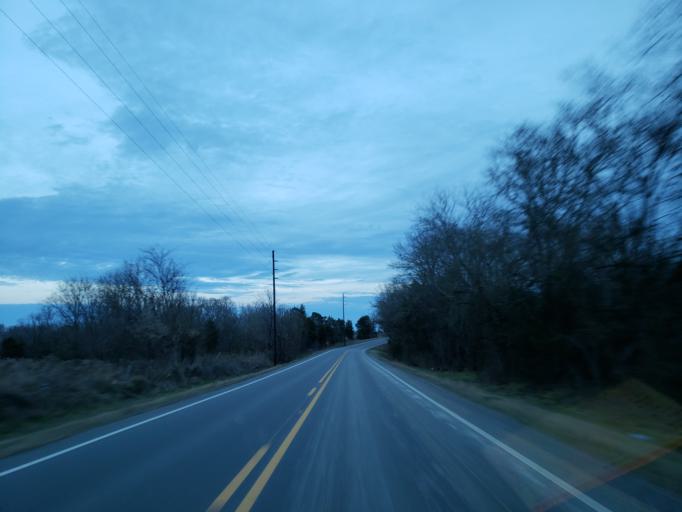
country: US
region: Alabama
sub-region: Sumter County
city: Livingston
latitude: 32.8119
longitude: -88.2816
